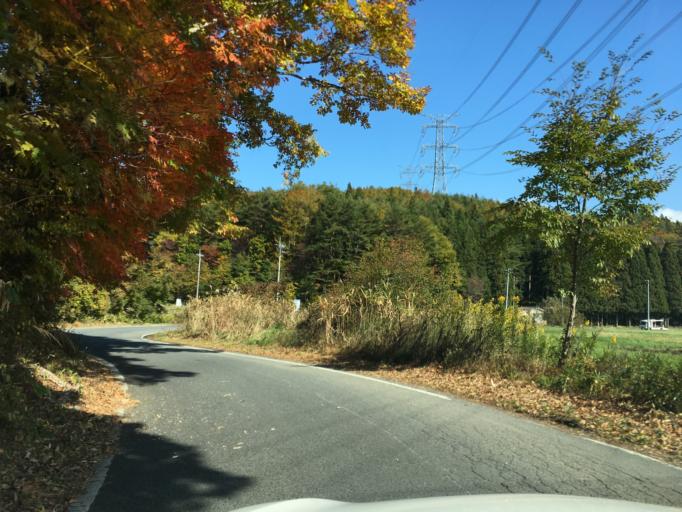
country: JP
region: Fukushima
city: Funehikimachi-funehiki
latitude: 37.2940
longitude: 140.7296
